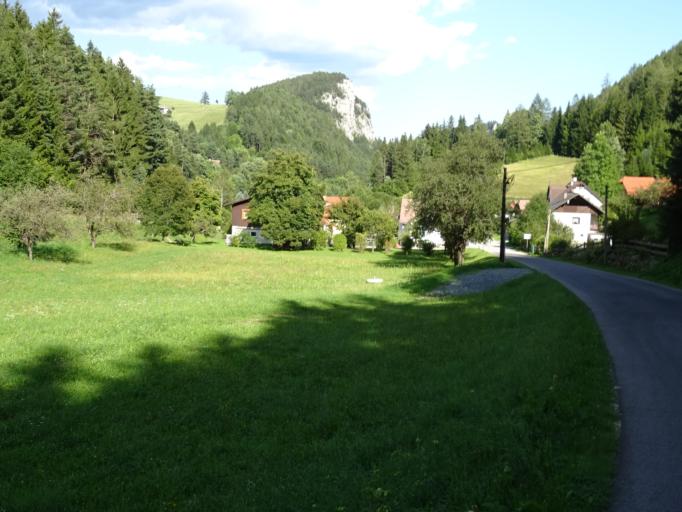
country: AT
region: Lower Austria
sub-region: Politischer Bezirk Neunkirchen
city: Semmering
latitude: 47.6571
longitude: 15.8148
